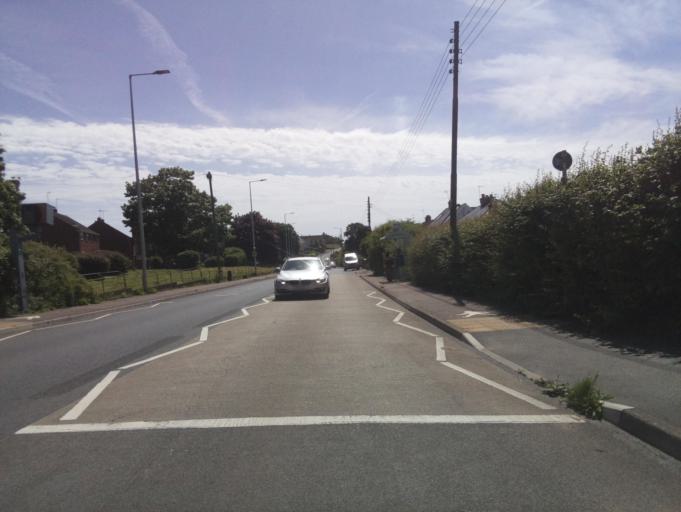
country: GB
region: England
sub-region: Devon
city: Exmouth
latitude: 50.6392
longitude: -3.4108
